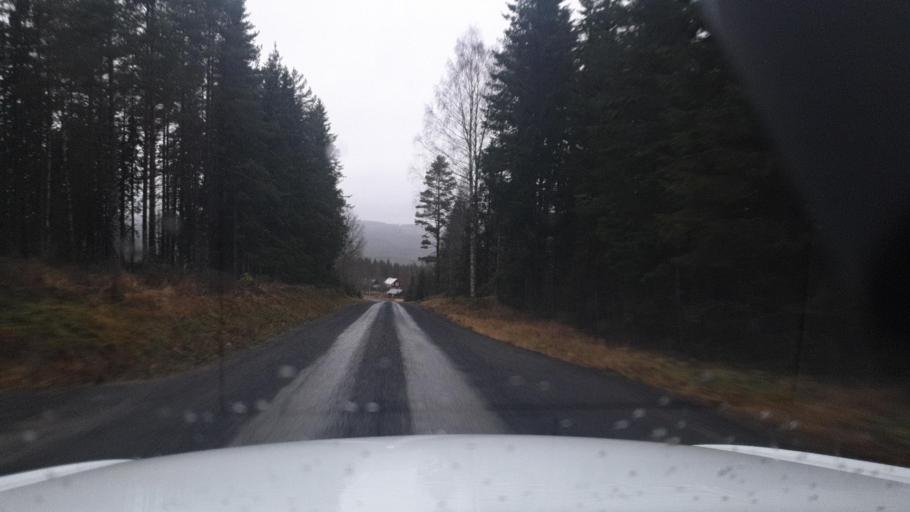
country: SE
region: Vaermland
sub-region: Torsby Kommun
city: Torsby
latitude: 60.1798
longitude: 12.6455
